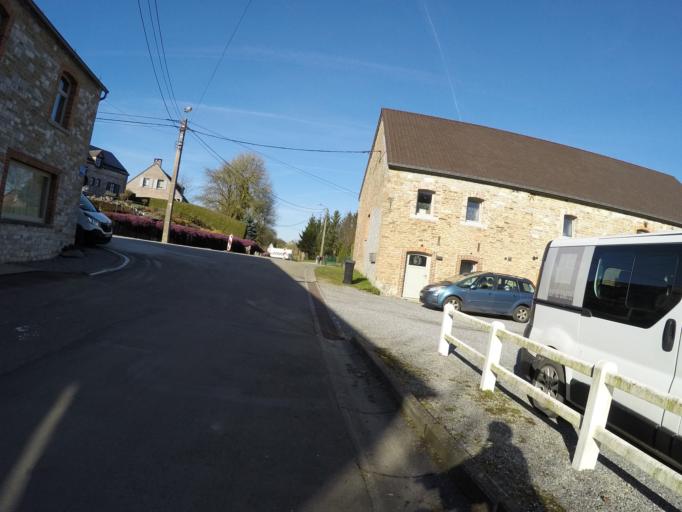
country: BE
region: Wallonia
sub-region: Province de Namur
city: Gesves
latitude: 50.3727
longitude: 5.0713
